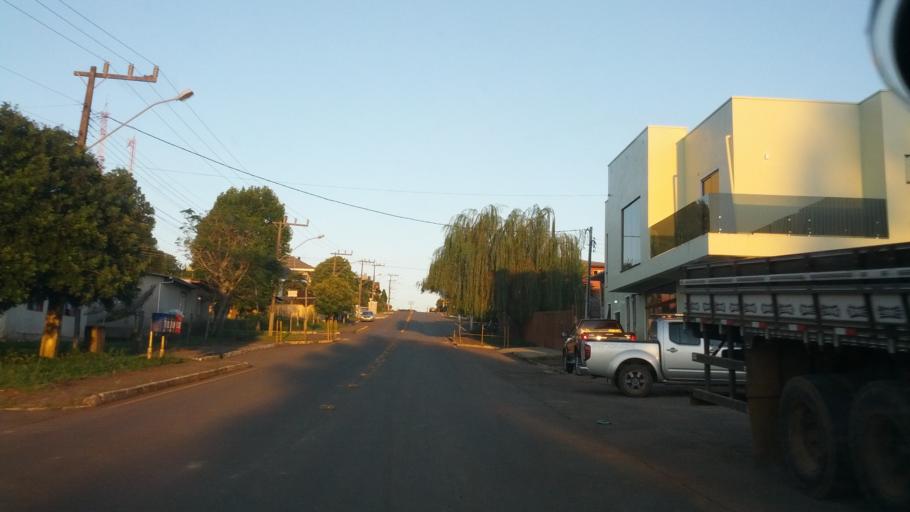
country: BR
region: Rio Grande do Sul
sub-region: Vacaria
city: Estrela
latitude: -27.7976
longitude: -50.8770
